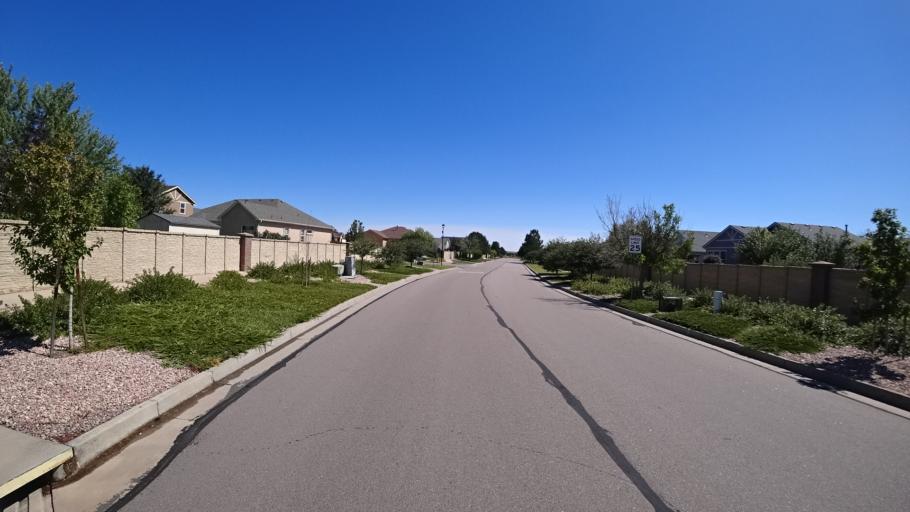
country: US
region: Colorado
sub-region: El Paso County
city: Security-Widefield
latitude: 38.7849
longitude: -104.7286
